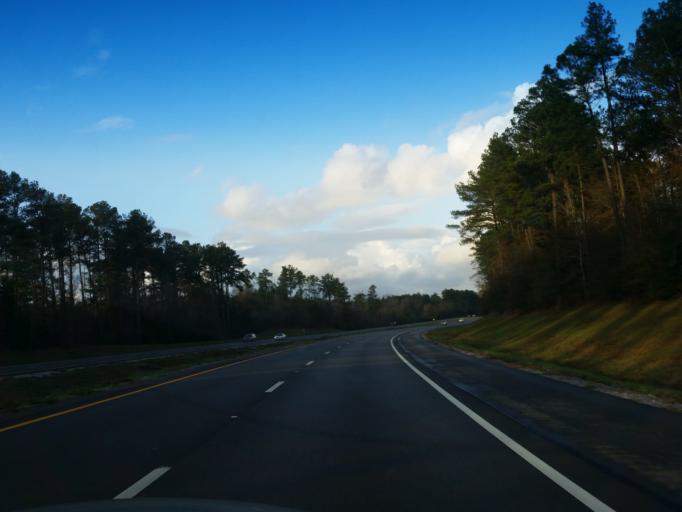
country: US
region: Mississippi
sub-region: Jones County
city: Sharon
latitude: 31.8730
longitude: -89.0452
